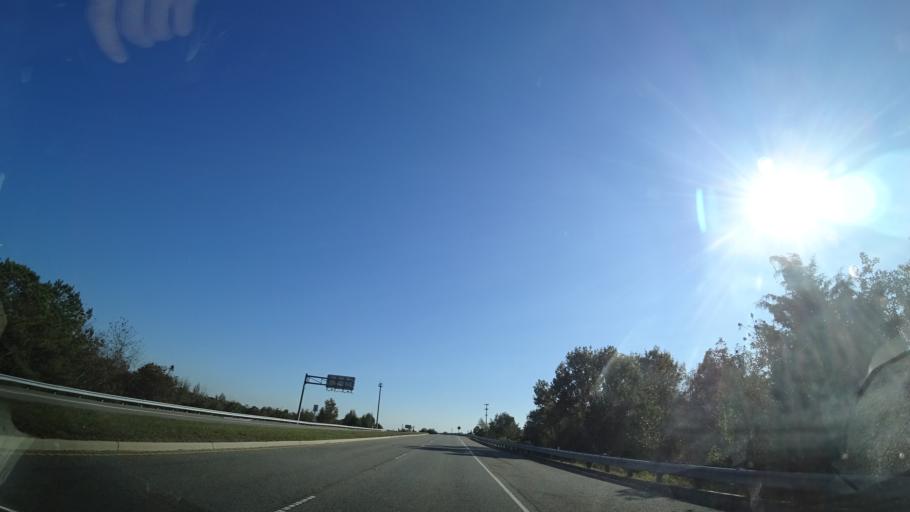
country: US
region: Virginia
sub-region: City of Newport News
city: Newport News
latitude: 36.8893
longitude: -76.4304
